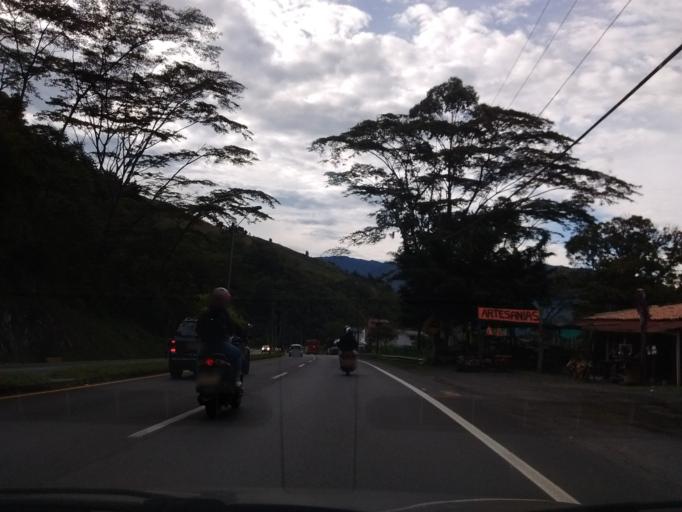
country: CO
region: Antioquia
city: Municipio de Copacabana
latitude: 6.3123
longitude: -75.5055
